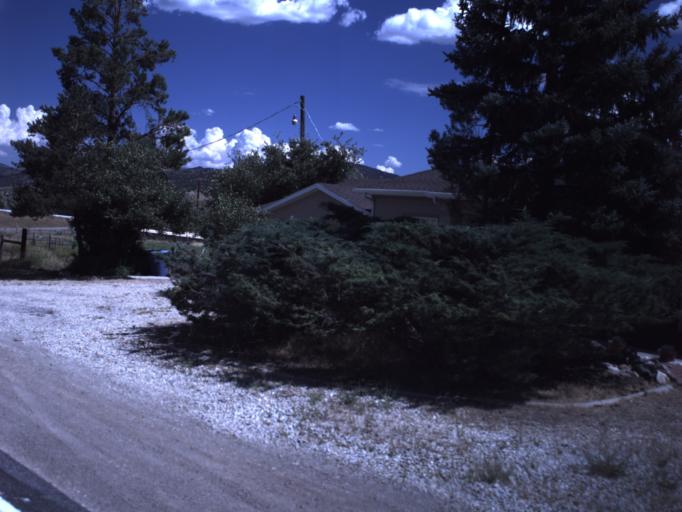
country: US
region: Utah
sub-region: Summit County
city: Coalville
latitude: 40.8059
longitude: -111.4078
